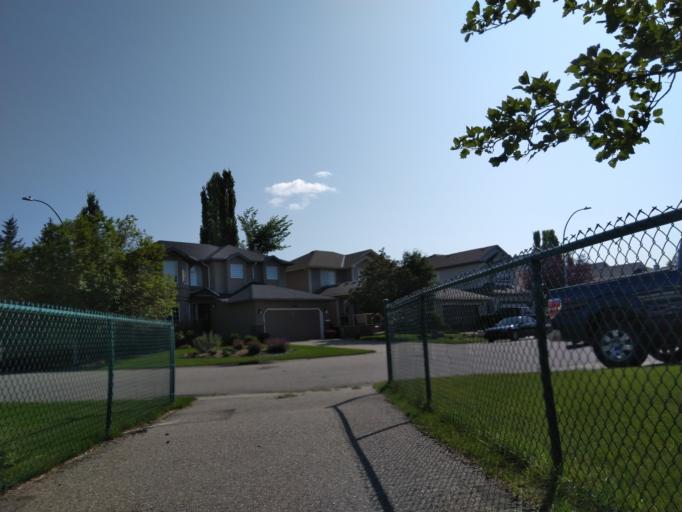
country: CA
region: Alberta
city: Calgary
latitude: 51.0955
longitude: -114.2478
